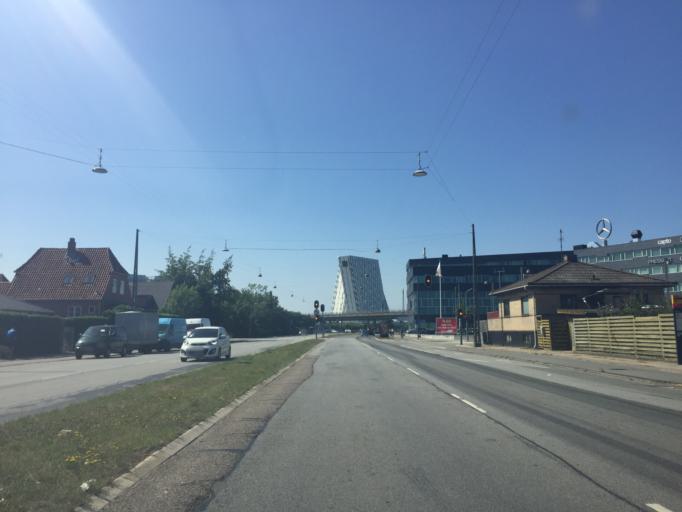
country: DK
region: Capital Region
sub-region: Tarnby Kommune
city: Tarnby
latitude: 55.6416
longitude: 12.5873
